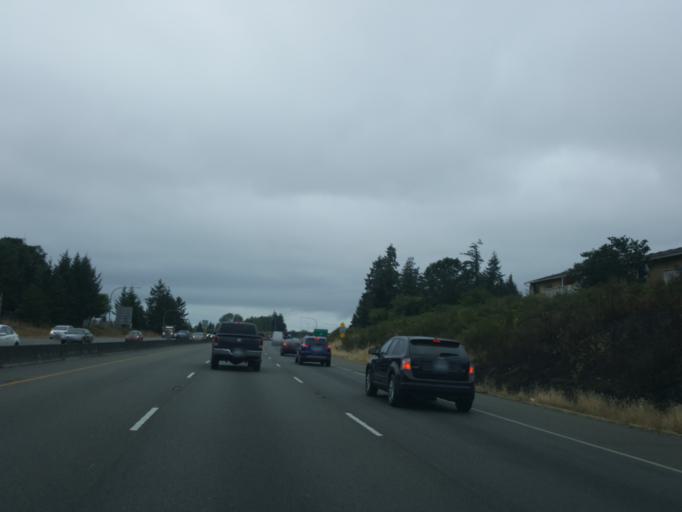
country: US
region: Washington
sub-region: Pierce County
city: Parkland
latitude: 47.1587
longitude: -122.4601
